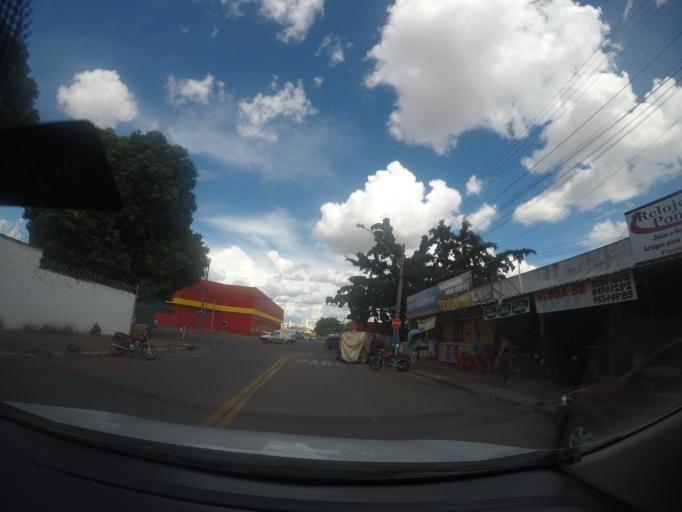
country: BR
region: Goias
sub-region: Goiania
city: Goiania
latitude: -16.6727
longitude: -49.3040
